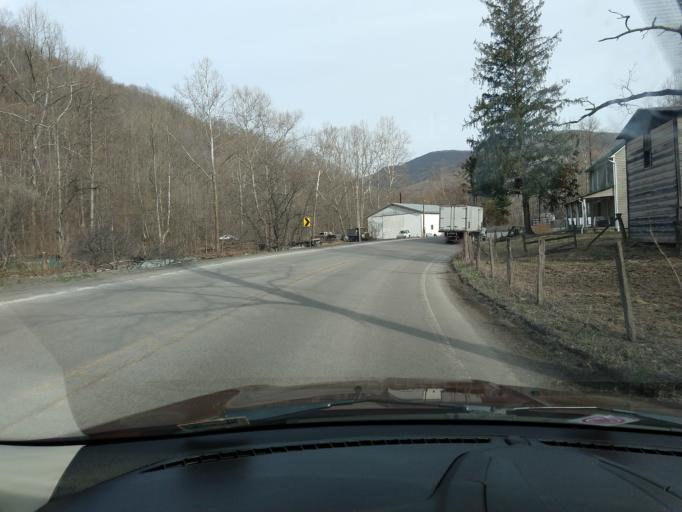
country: US
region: West Virginia
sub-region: Pendleton County
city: Franklin
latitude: 38.8446
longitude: -79.4220
